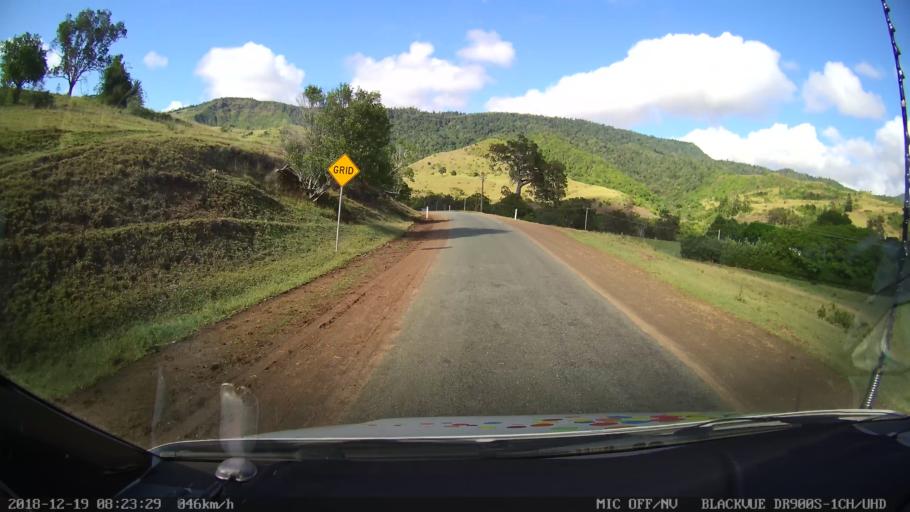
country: AU
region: New South Wales
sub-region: Kyogle
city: Kyogle
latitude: -28.3069
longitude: 152.9085
